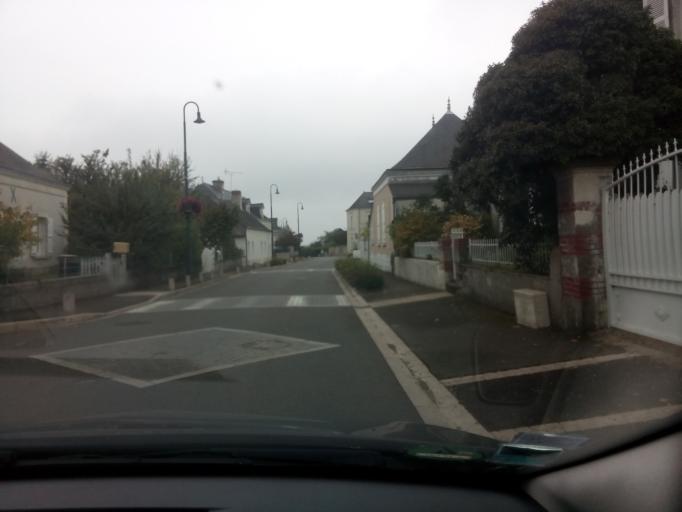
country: FR
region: Pays de la Loire
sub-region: Departement de Maine-et-Loire
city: Soulaire-et-Bourg
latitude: 47.5784
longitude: -0.5539
